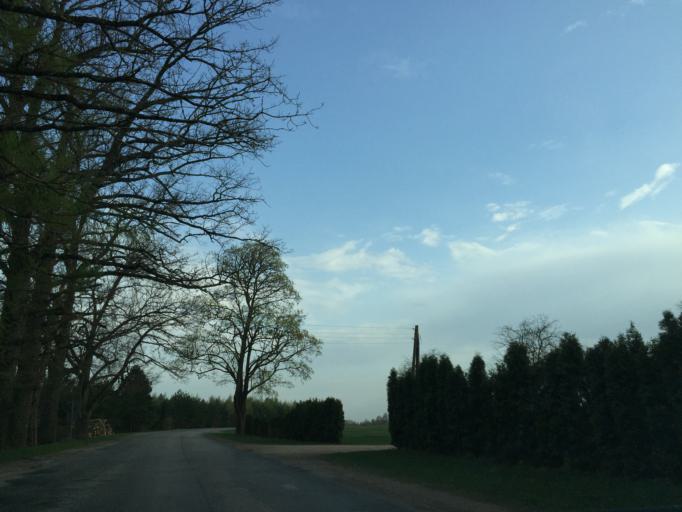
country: LV
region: Malpils
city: Malpils
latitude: 57.0051
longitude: 24.9117
